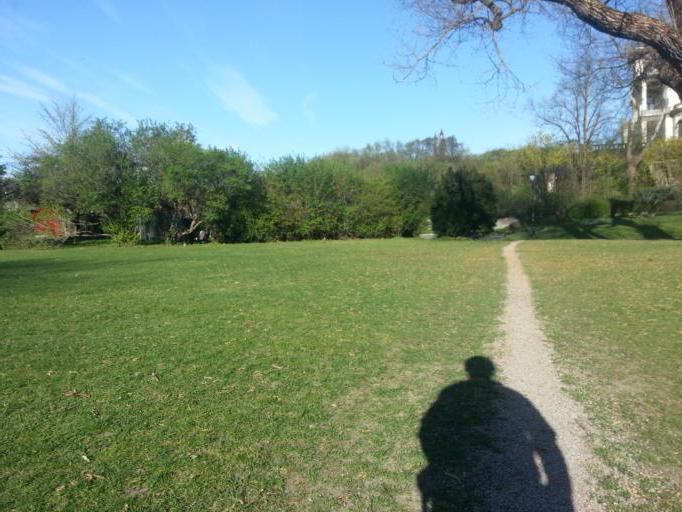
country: NO
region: Oslo
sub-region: Oslo
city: Sjolyststranda
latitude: 59.9148
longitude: 10.7009
